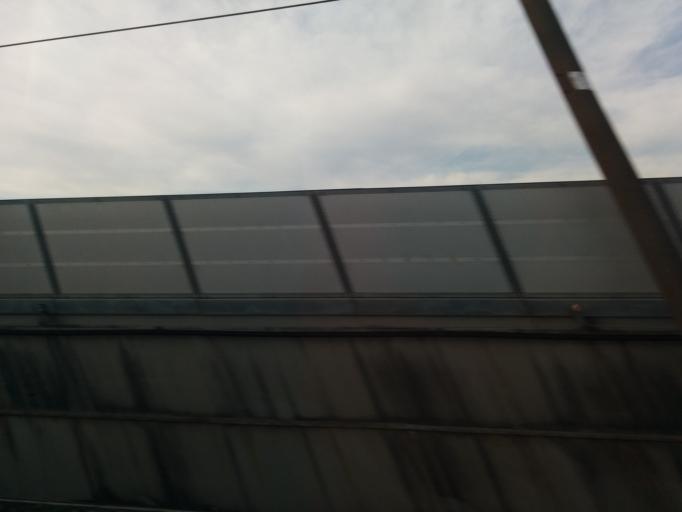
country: JP
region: Shiga Prefecture
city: Kusatsu
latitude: 35.0059
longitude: 135.9685
